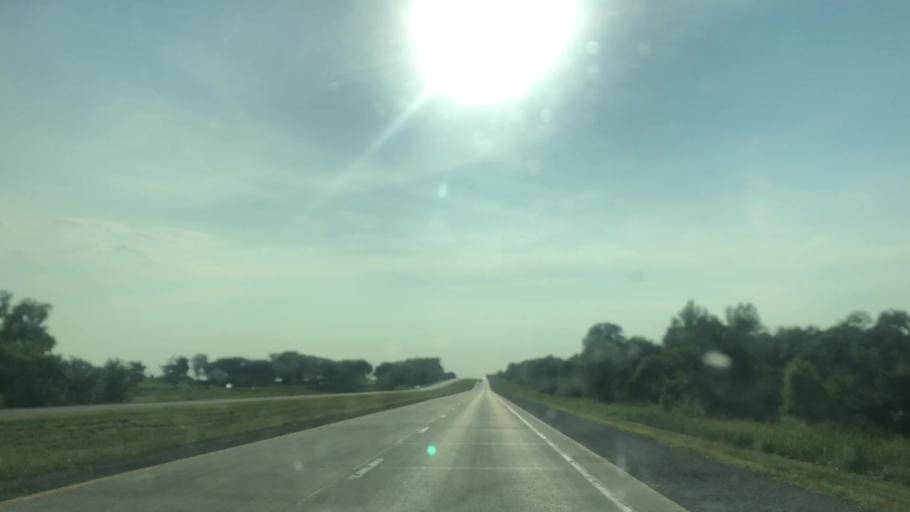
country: US
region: Iowa
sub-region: Story County
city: Nevada
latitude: 42.0077
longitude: -93.3804
